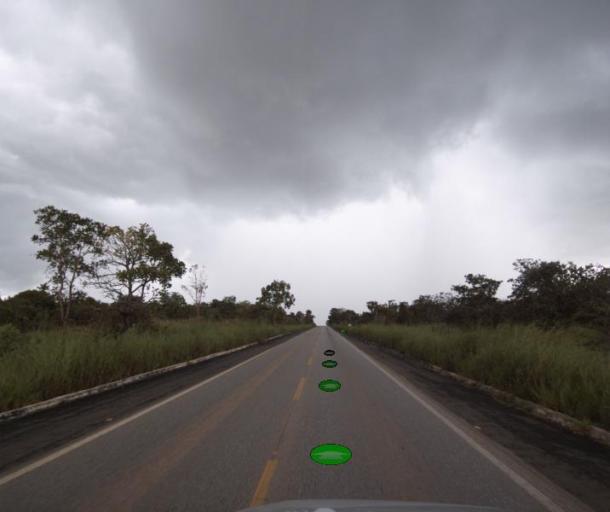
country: BR
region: Goias
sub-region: Uruacu
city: Uruacu
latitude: -14.2152
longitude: -49.1314
